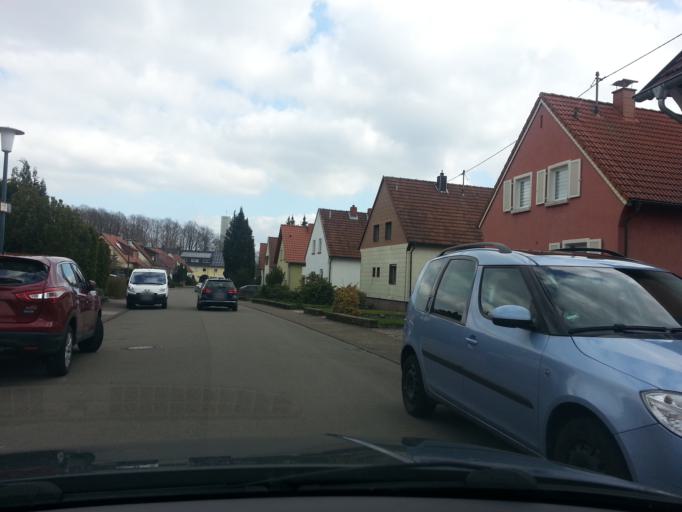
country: DE
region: Saarland
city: Neunkirchen
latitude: 49.3256
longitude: 7.2174
